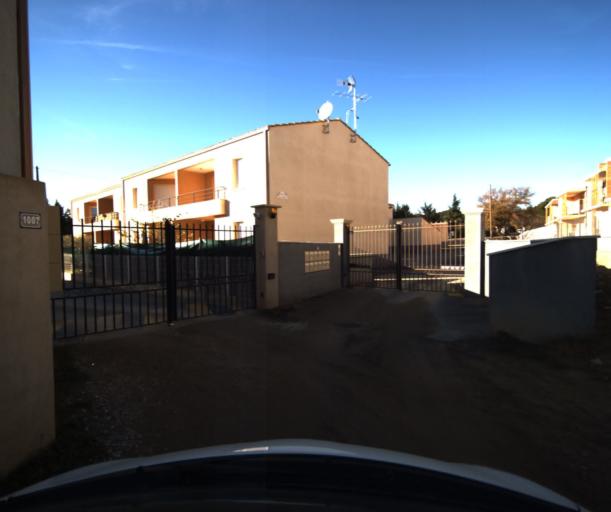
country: FR
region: Provence-Alpes-Cote d'Azur
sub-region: Departement du Vaucluse
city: Pertuis
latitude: 43.7050
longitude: 5.4957
